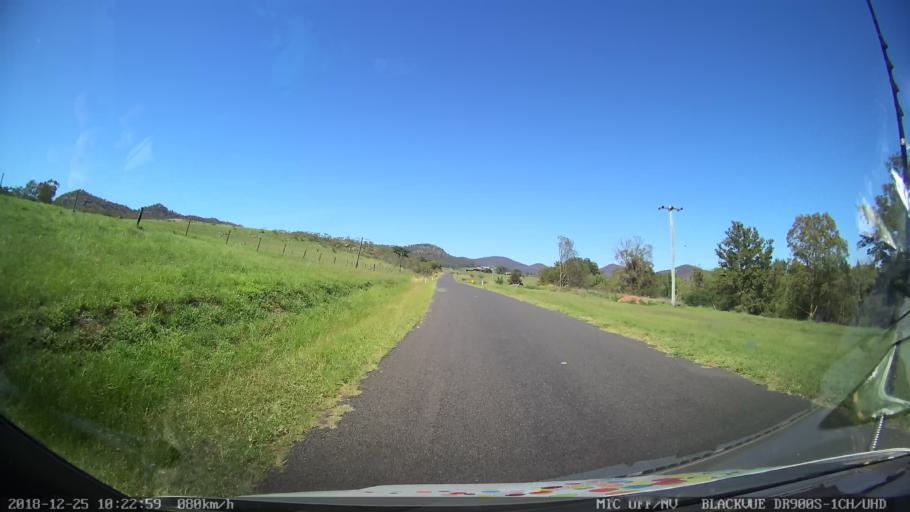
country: AU
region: New South Wales
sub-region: Muswellbrook
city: Denman
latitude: -32.3810
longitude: 150.5263
